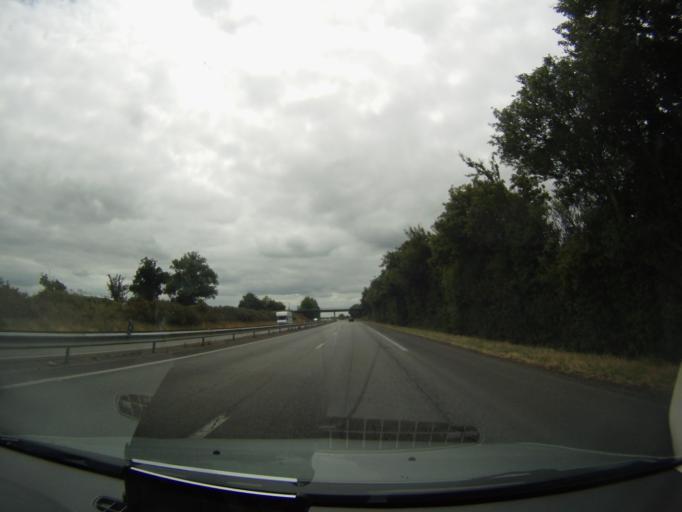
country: FR
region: Pays de la Loire
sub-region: Departement de la Loire-Atlantique
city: Heric
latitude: 47.4489
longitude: -1.6415
